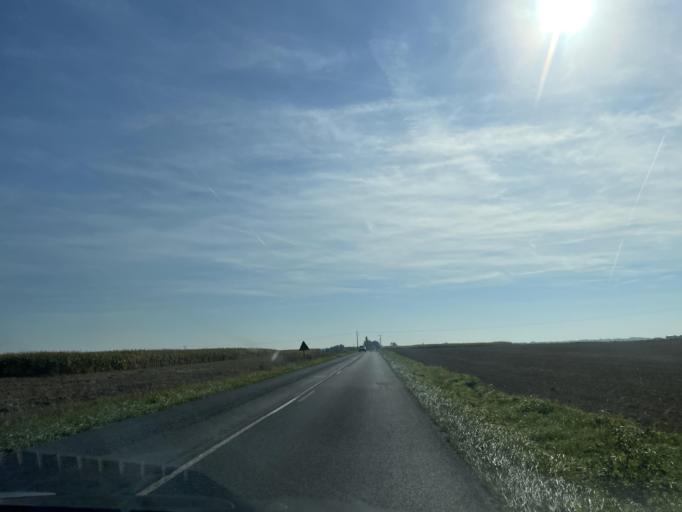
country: FR
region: Ile-de-France
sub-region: Departement de Seine-et-Marne
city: Sammeron
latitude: 48.8827
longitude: 3.0709
